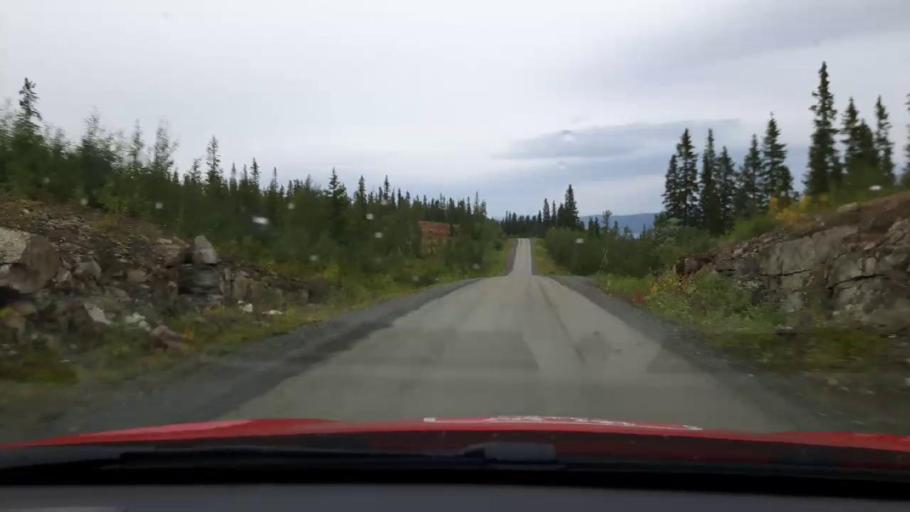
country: SE
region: Jaemtland
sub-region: Are Kommun
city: Are
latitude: 63.4141
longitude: 13.2330
